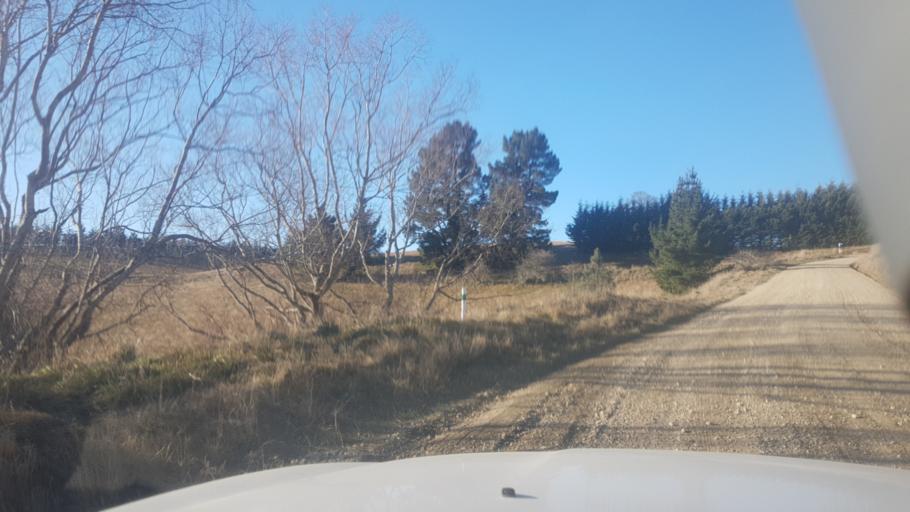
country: NZ
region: Canterbury
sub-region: Timaru District
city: Pleasant Point
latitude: -44.3429
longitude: 171.0698
